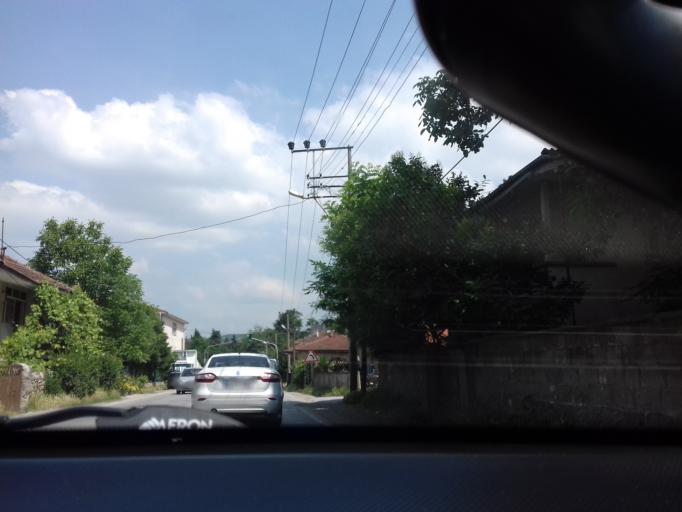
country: TR
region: Sakarya
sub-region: Merkez
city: Sapanca
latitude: 40.6878
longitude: 30.2664
